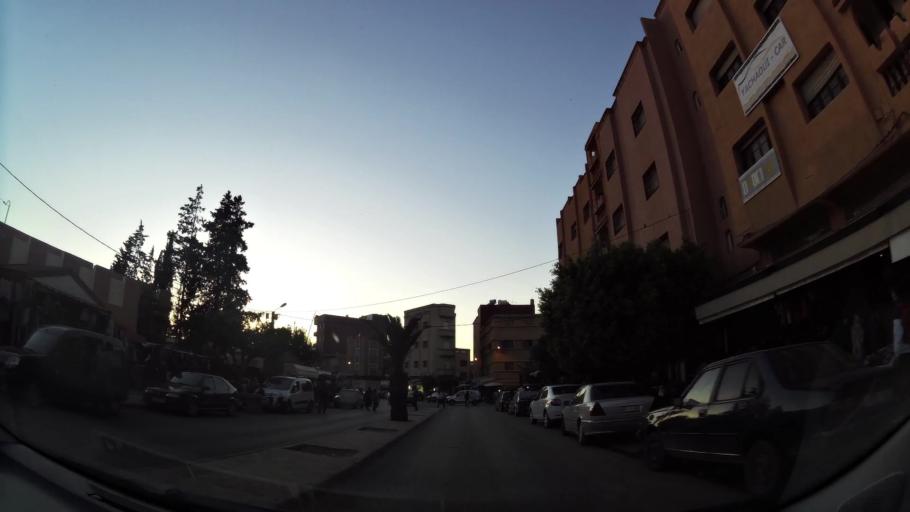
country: MA
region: Oriental
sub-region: Berkane-Taourirt
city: Berkane
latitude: 34.9210
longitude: -2.3220
